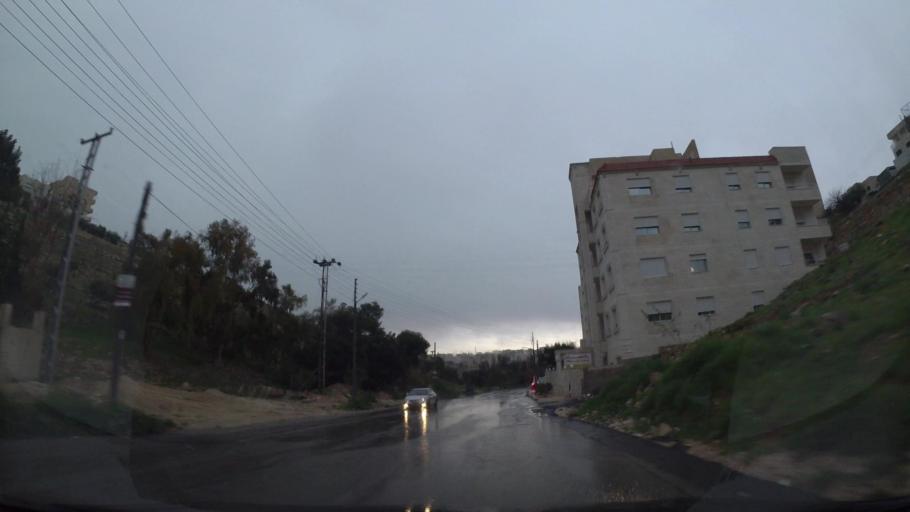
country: JO
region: Amman
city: Amman
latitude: 31.9928
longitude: 35.9731
